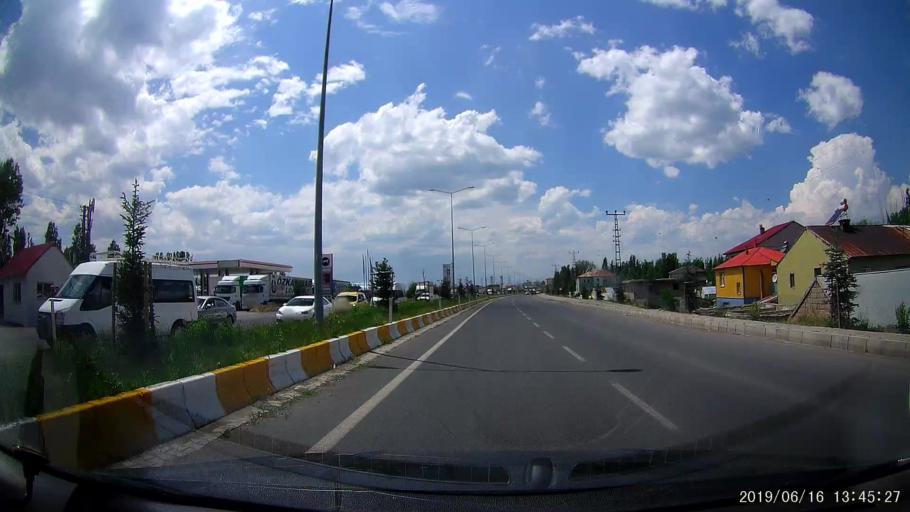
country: TR
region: Agri
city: Agri
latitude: 39.7088
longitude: 43.0457
